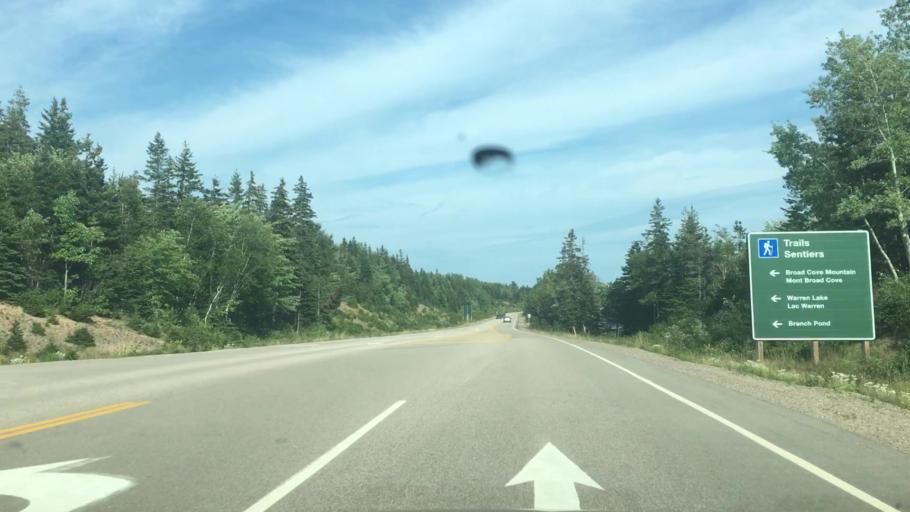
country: CA
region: Nova Scotia
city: Sydney Mines
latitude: 46.7124
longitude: -60.3651
